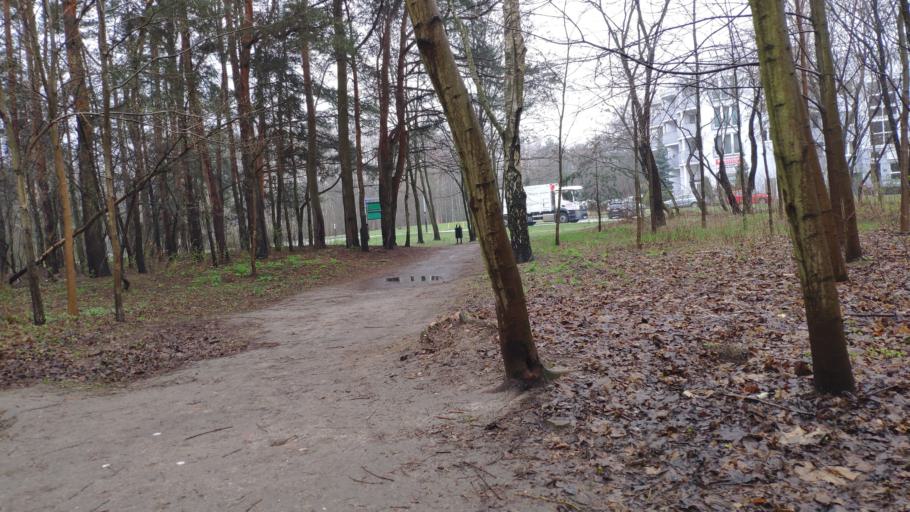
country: PL
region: Lodz Voivodeship
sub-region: Powiat lodzki wschodni
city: Andrespol
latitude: 51.7520
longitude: 19.5664
